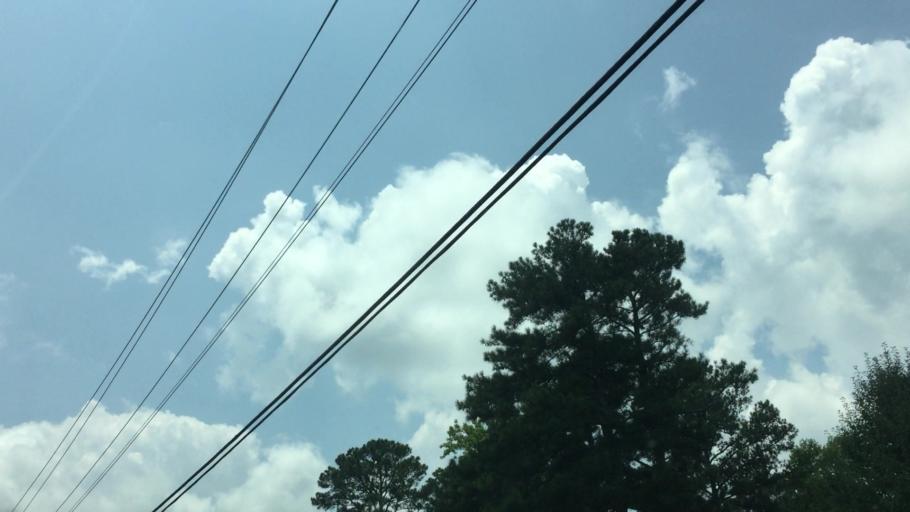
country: US
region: Georgia
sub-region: Carroll County
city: Villa Rica
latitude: 33.6136
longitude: -84.8903
